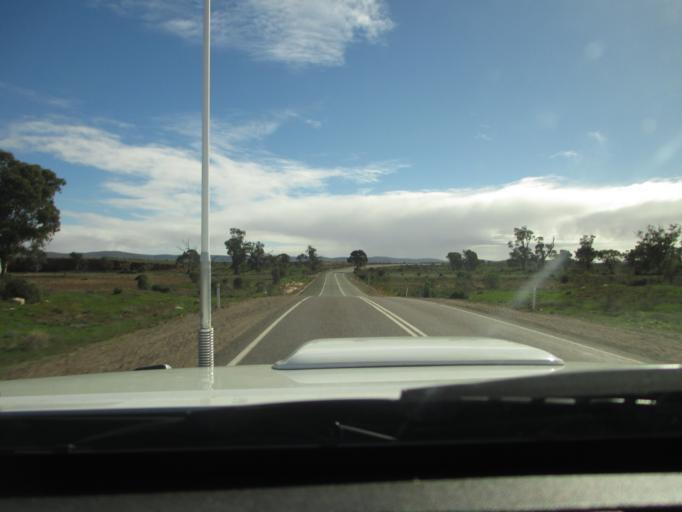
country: AU
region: South Australia
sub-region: Flinders Ranges
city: Quorn
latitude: -31.7634
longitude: 138.3316
